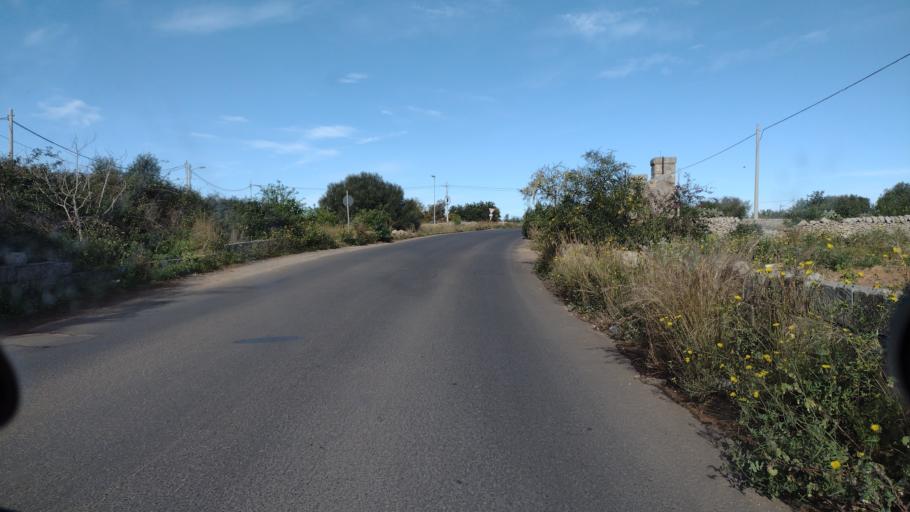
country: IT
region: Sicily
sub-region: Provincia di Siracusa
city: Avola
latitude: 36.8735
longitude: 15.1171
